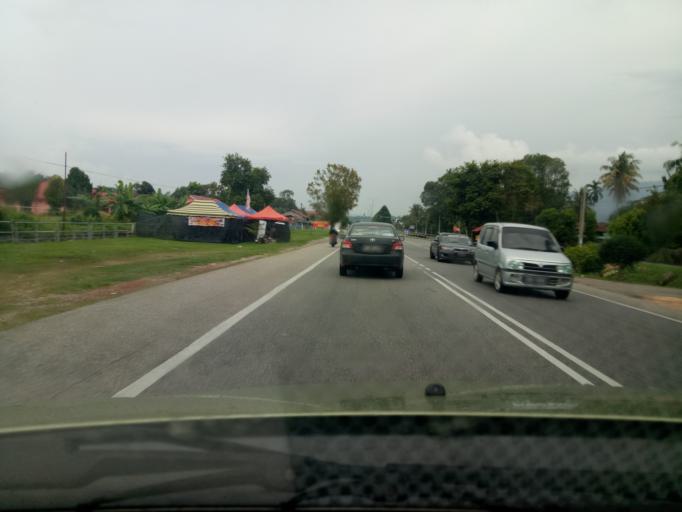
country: MY
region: Kedah
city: Gurun
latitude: 5.8655
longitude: 100.4545
